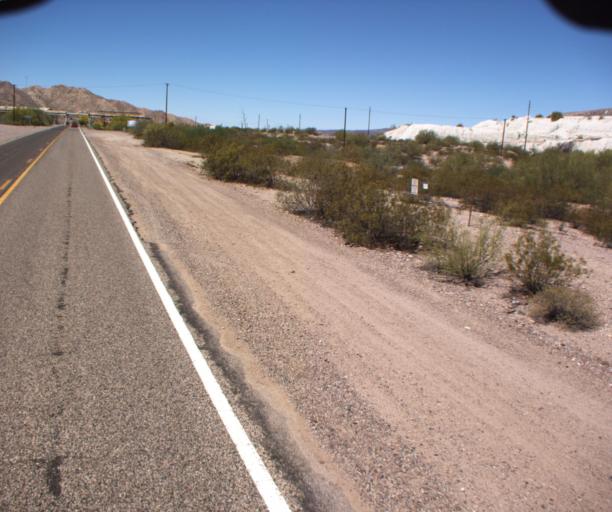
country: US
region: Arizona
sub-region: Pima County
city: Ajo
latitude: 32.3688
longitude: -112.8493
